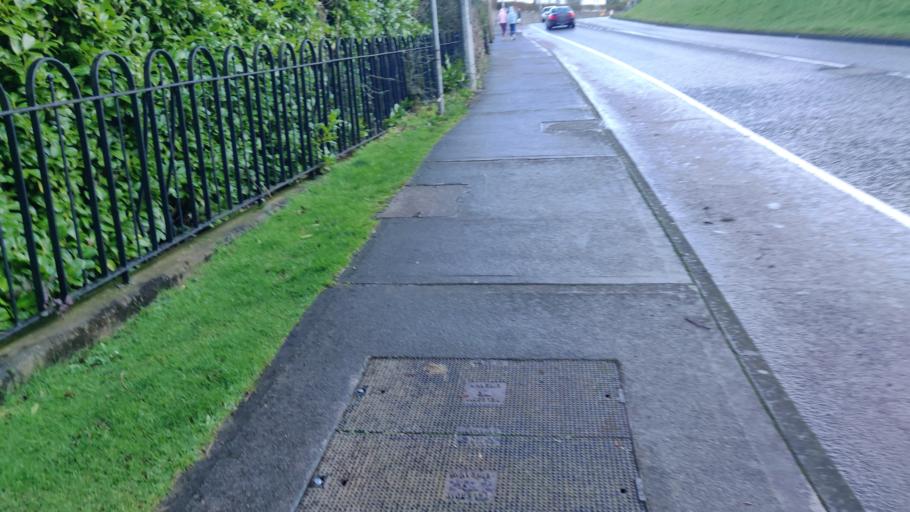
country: IE
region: Munster
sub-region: County Cork
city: Cork
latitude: 51.8723
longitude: -8.4213
